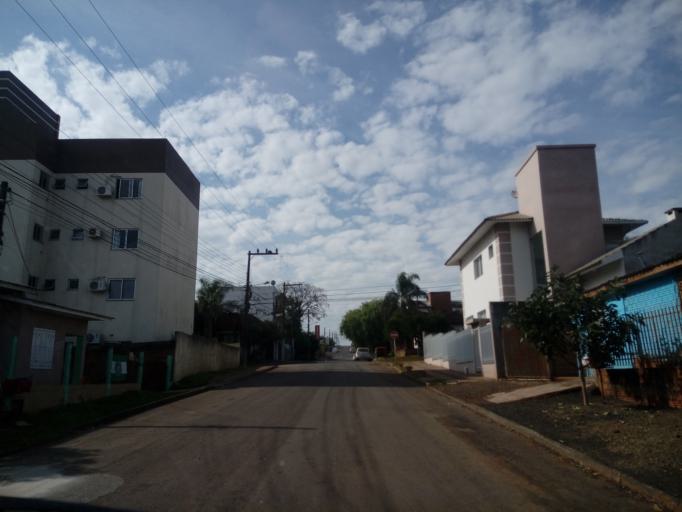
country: BR
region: Santa Catarina
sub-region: Chapeco
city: Chapeco
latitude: -27.1190
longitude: -52.6257
